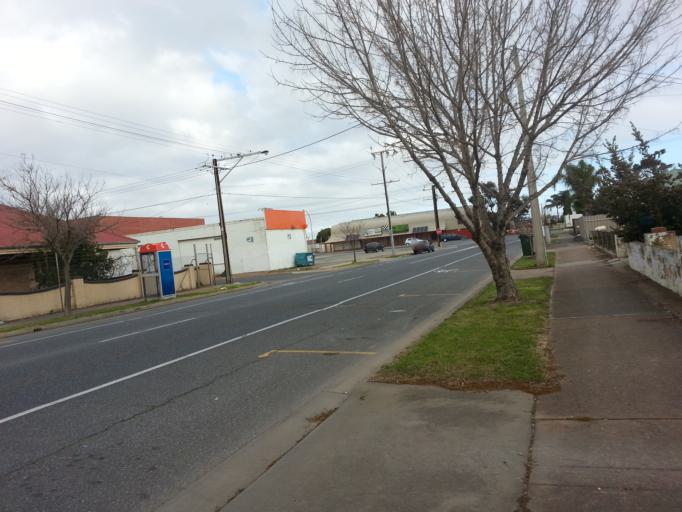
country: AU
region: South Australia
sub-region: Port Adelaide Enfield
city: Alberton
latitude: -34.8511
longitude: 138.5168
